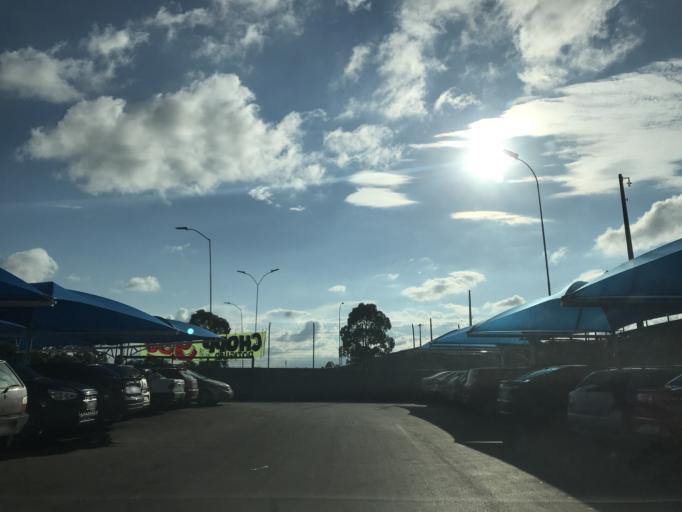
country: BR
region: Federal District
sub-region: Brasilia
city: Brasilia
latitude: -15.6548
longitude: -47.7819
